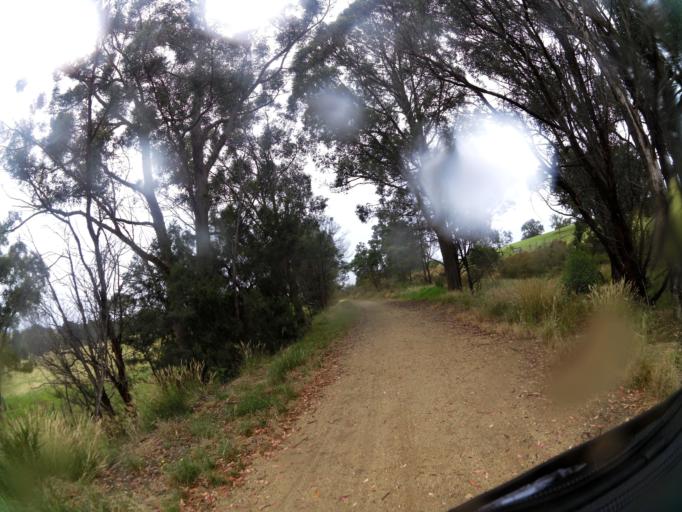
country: AU
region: Victoria
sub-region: East Gippsland
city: Lakes Entrance
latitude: -37.7618
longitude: 147.8183
